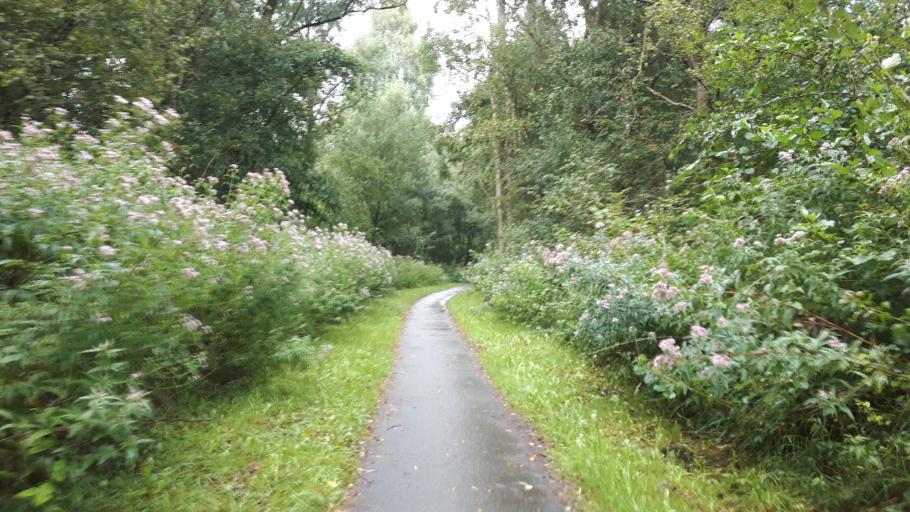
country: NL
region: Overijssel
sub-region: Gemeente Steenwijkerland
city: Blokzijl
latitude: 52.7699
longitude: 5.9645
